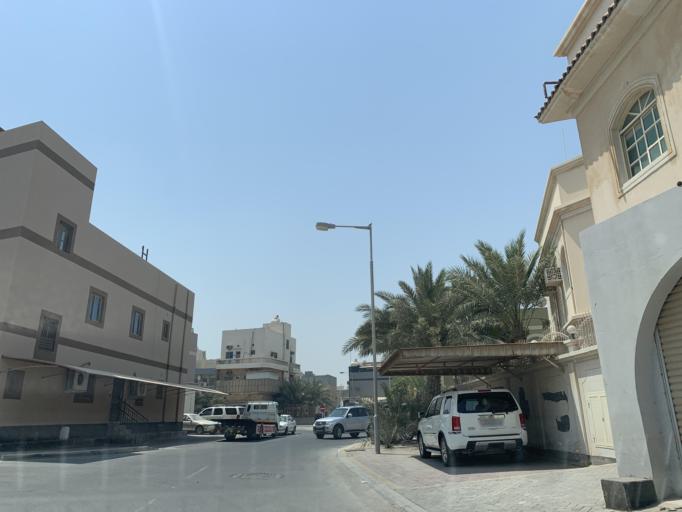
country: BH
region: Manama
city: Jidd Hafs
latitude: 26.2058
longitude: 50.5195
